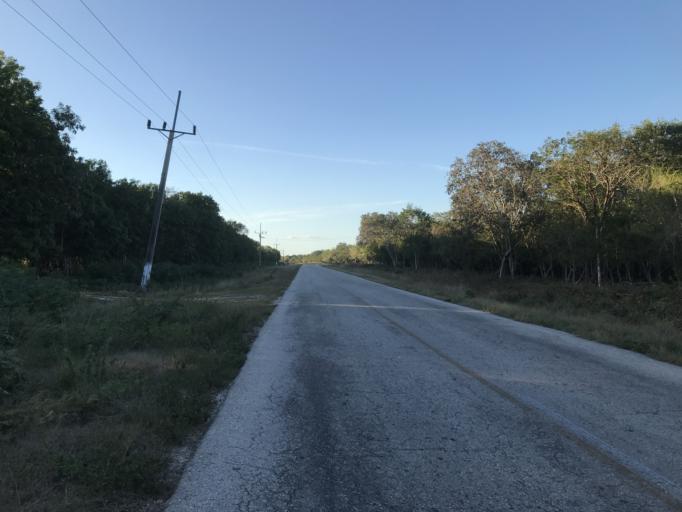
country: CU
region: Cienfuegos
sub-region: Municipio de Aguada de Pasajeros
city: Aguada de Pasajeros
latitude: 22.0706
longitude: -81.0538
